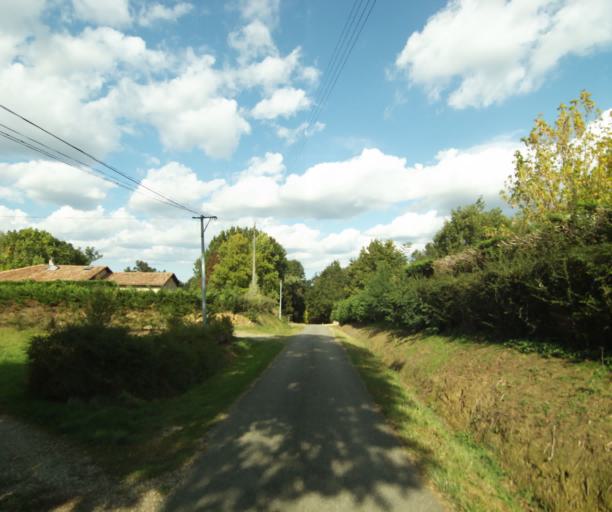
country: FR
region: Midi-Pyrenees
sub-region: Departement du Gers
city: Cazaubon
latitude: 43.9317
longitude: -0.0440
